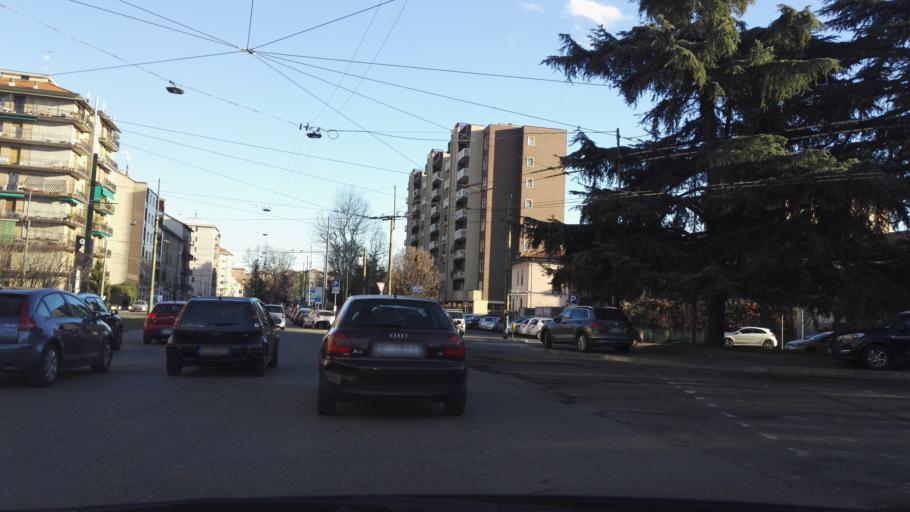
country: IT
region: Lombardy
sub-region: Citta metropolitana di Milano
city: Romano Banco
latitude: 45.4700
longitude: 9.1236
